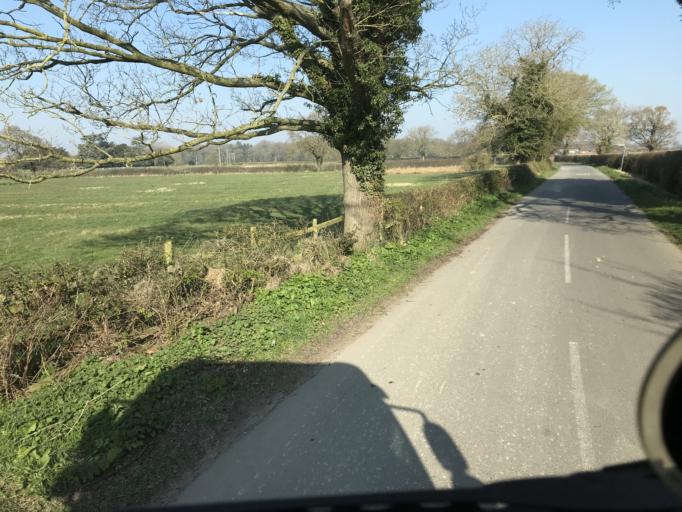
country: GB
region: England
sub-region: Cheshire West and Chester
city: Aldford
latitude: 53.1380
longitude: -2.8372
